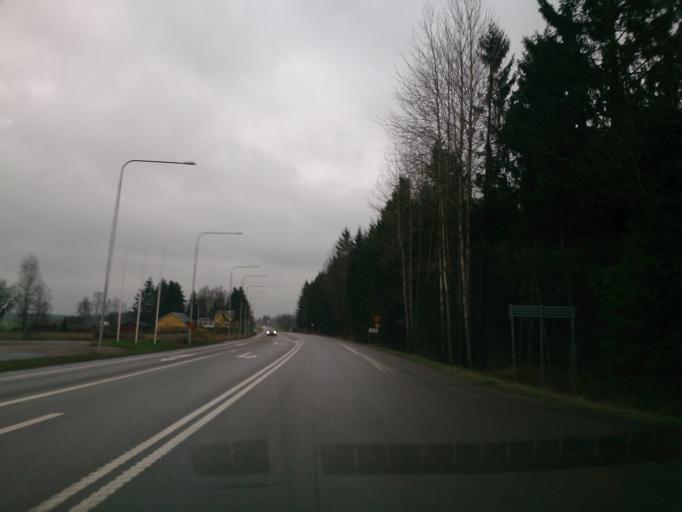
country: SE
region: OEstergoetland
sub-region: Linkopings Kommun
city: Linghem
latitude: 58.4396
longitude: 15.8033
